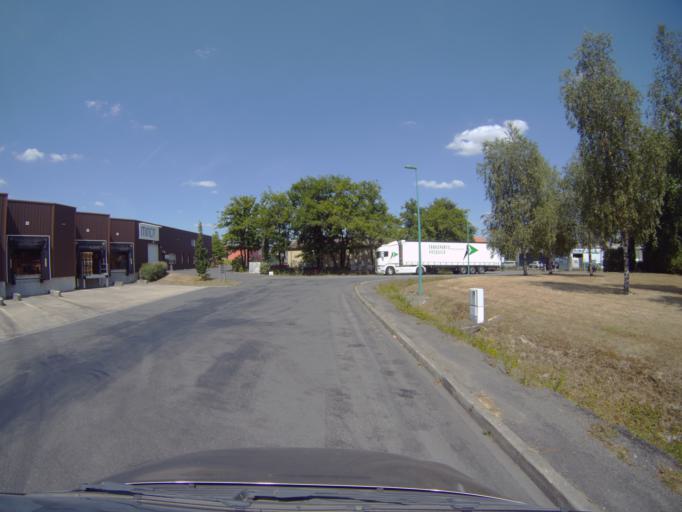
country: FR
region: Pays de la Loire
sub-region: Departement de la Loire-Atlantique
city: Aigrefeuille-sur-Maine
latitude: 47.0808
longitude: -1.4142
